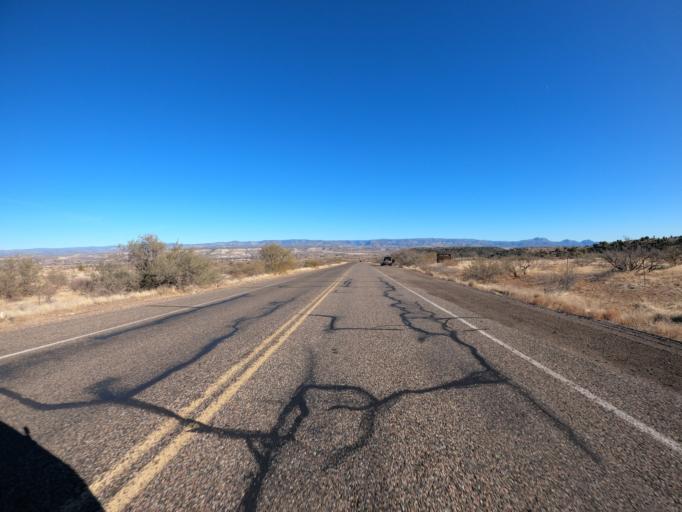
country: US
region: Arizona
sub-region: Yavapai County
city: Camp Verde
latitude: 34.5590
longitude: -111.9004
